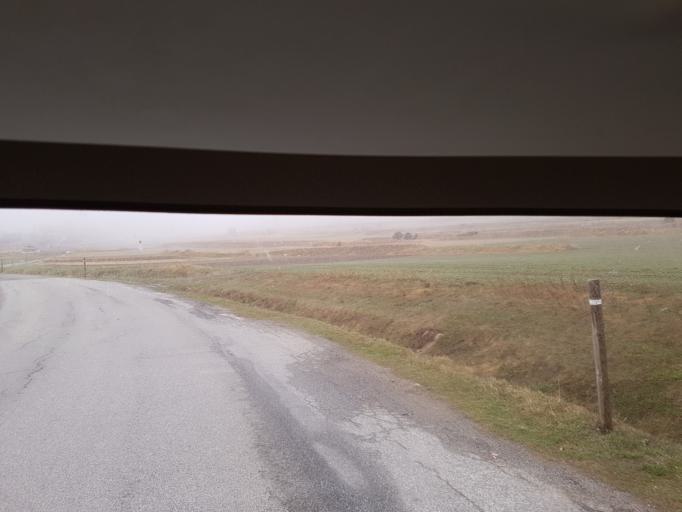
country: ES
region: Catalonia
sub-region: Provincia de Girona
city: Llivia
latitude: 42.5856
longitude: 2.0859
